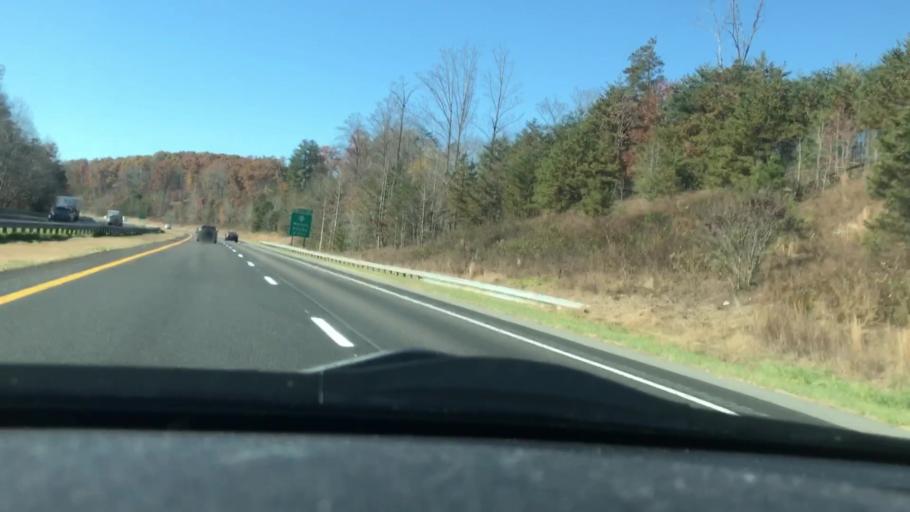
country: US
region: North Carolina
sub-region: McDowell County
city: Marion
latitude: 35.6794
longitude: -81.9338
